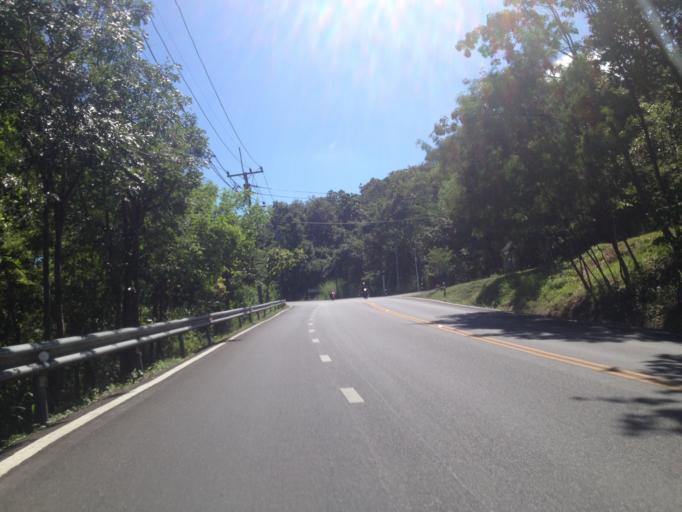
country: TH
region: Chiang Mai
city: Chiang Mai
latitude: 18.8091
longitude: 98.9377
